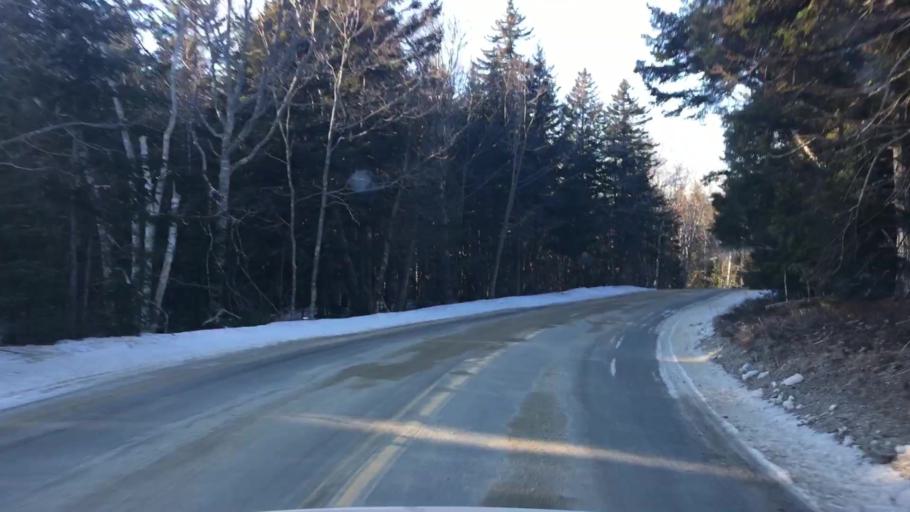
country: US
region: Maine
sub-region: Hancock County
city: Castine
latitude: 44.3662
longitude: -68.7522
